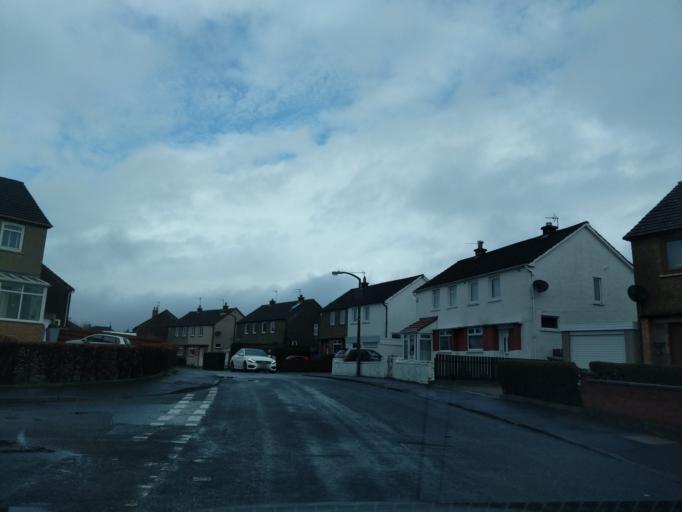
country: GB
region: Scotland
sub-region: Edinburgh
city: Colinton
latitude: 55.9372
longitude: -3.2860
